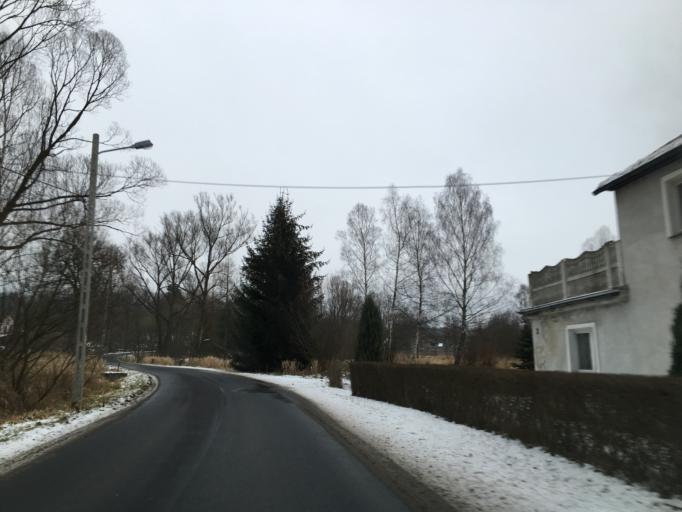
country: PL
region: Lower Silesian Voivodeship
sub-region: Powiat walbrzyski
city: Mieroszow
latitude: 50.7020
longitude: 16.1362
